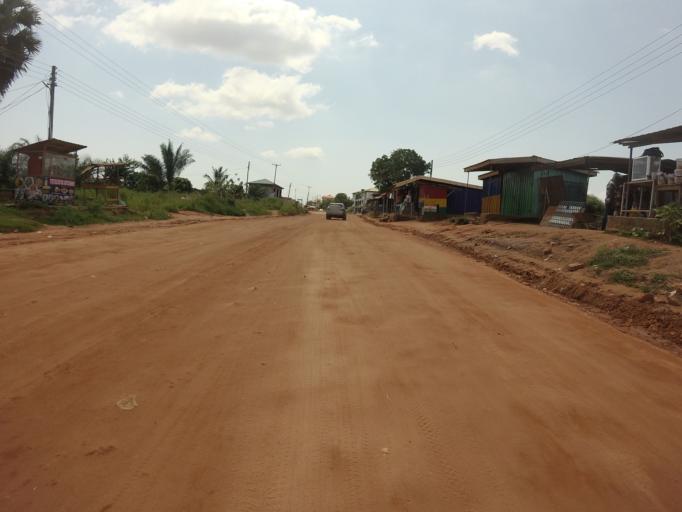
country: GH
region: Greater Accra
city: Gbawe
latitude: 5.6176
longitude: -0.3106
